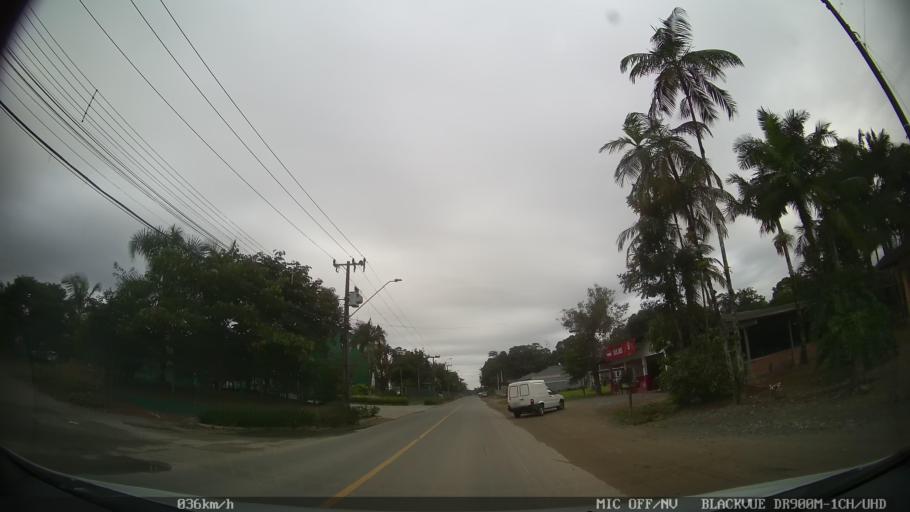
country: BR
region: Santa Catarina
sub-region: Joinville
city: Joinville
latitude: -26.2601
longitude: -48.9247
